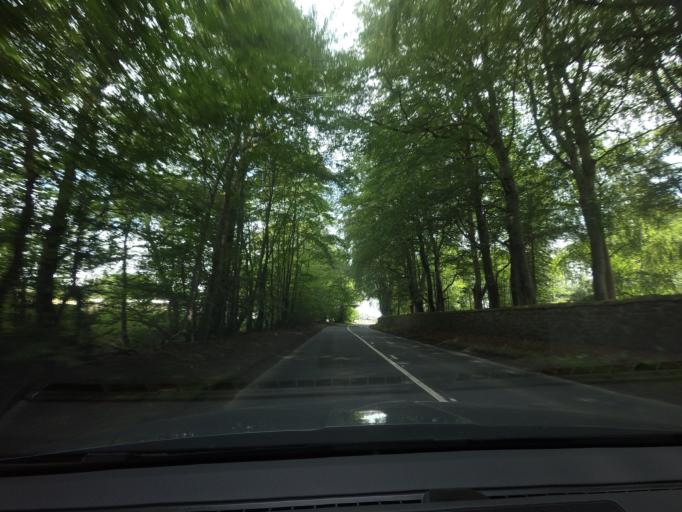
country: GB
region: Scotland
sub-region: Aberdeenshire
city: Mintlaw
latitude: 57.5261
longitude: -2.0289
